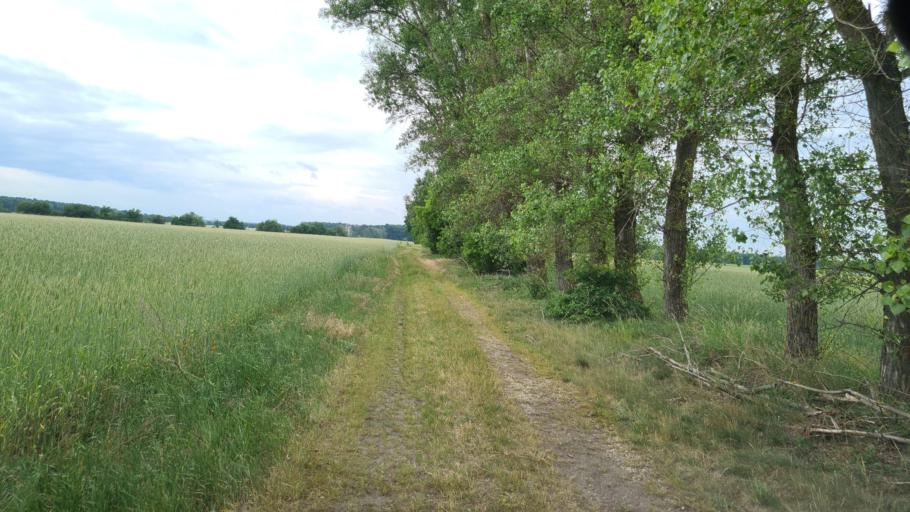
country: DE
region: Brandenburg
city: Bronkow
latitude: 51.6268
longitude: 13.9372
